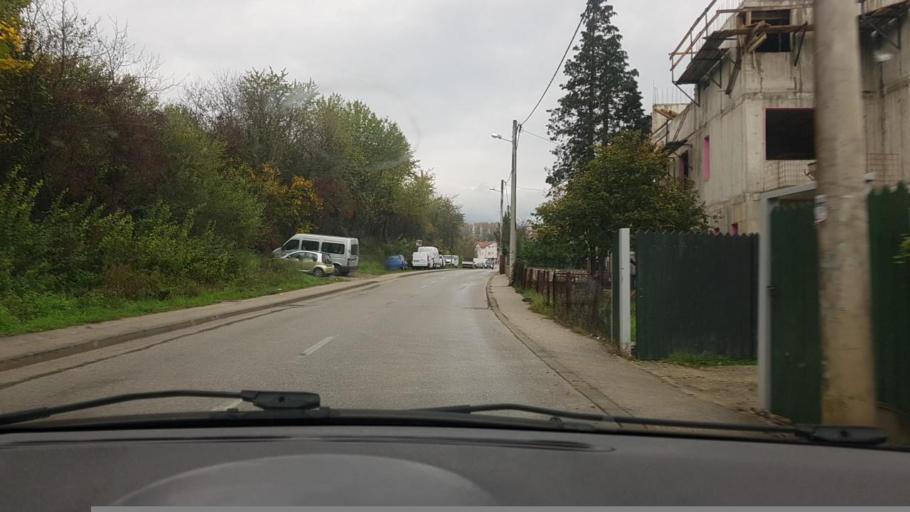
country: HR
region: Grad Zagreb
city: Zagreb
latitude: 45.8299
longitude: 16.0055
